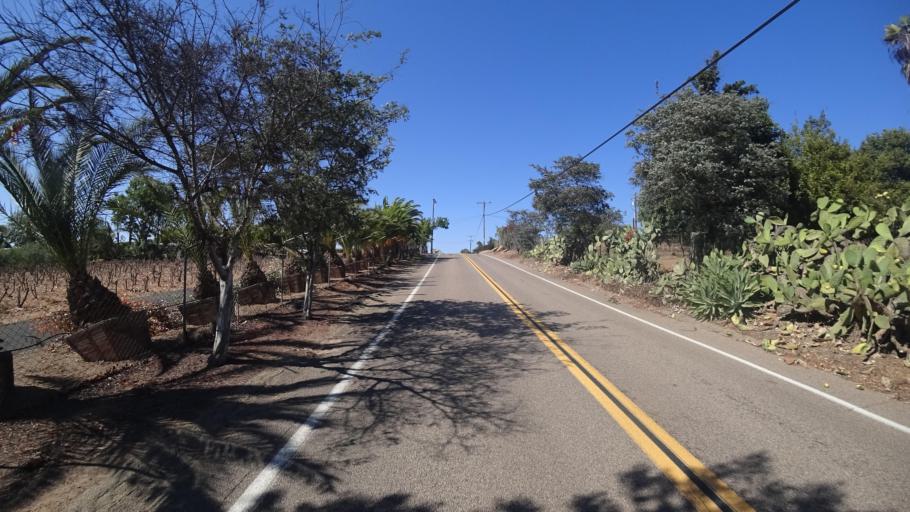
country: US
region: California
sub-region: San Diego County
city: Hidden Meadows
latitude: 33.2705
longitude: -117.1122
